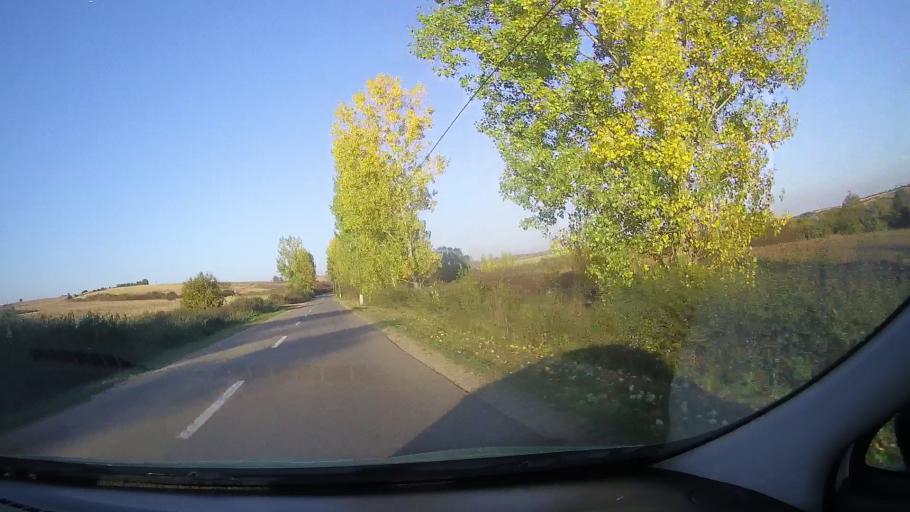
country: RO
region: Bihor
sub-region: Comuna Paleu
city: Paleu
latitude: 47.1235
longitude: 21.9627
